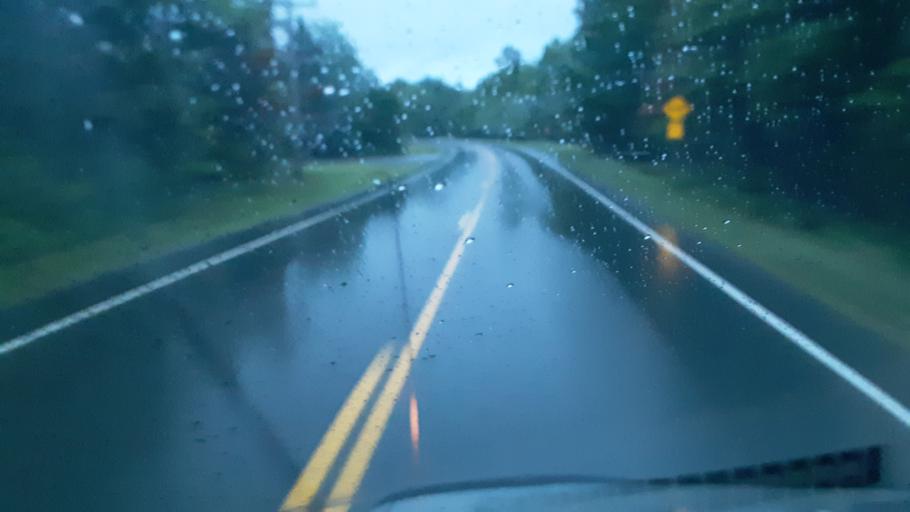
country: US
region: Maine
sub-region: Penobscot County
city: Patten
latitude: 45.9315
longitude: -68.4479
